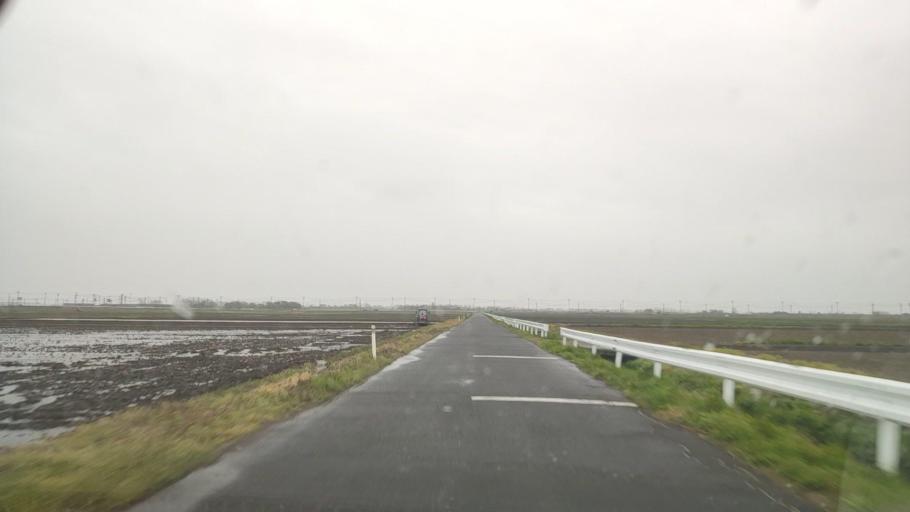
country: JP
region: Akita
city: Noshiromachi
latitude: 40.1021
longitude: 139.9977
